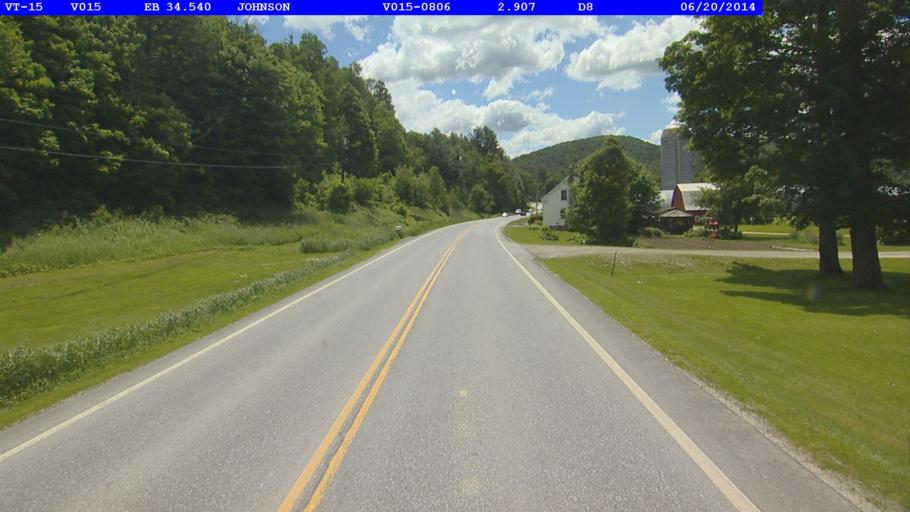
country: US
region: Vermont
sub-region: Lamoille County
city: Johnson
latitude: 44.6398
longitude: -72.7001
